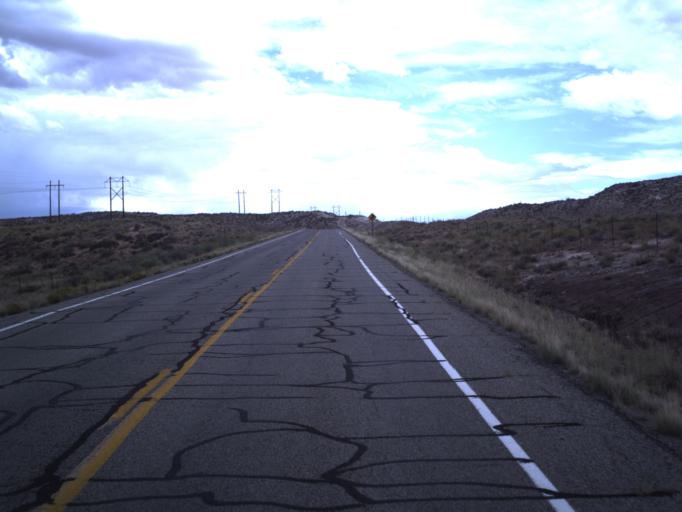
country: US
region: Utah
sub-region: San Juan County
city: Blanding
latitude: 37.2868
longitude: -109.3905
